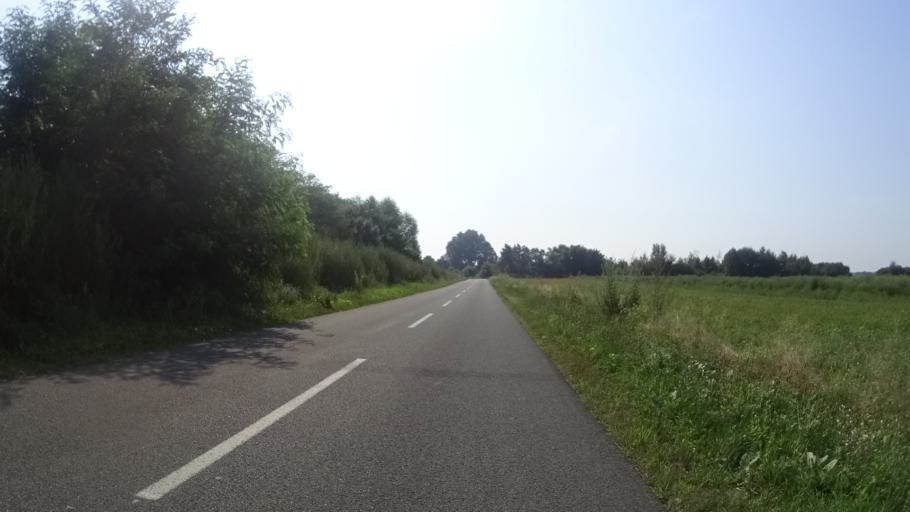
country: HR
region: Medimurska
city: Belica
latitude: 46.3936
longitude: 16.5308
